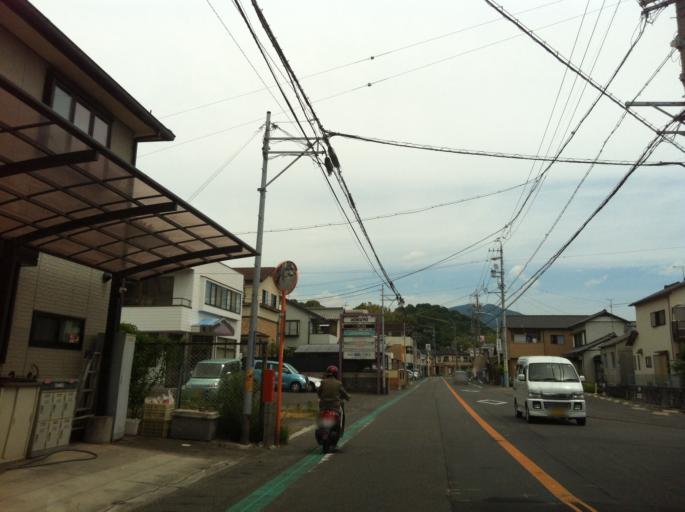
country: JP
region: Shizuoka
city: Shizuoka-shi
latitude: 35.0114
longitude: 138.4131
